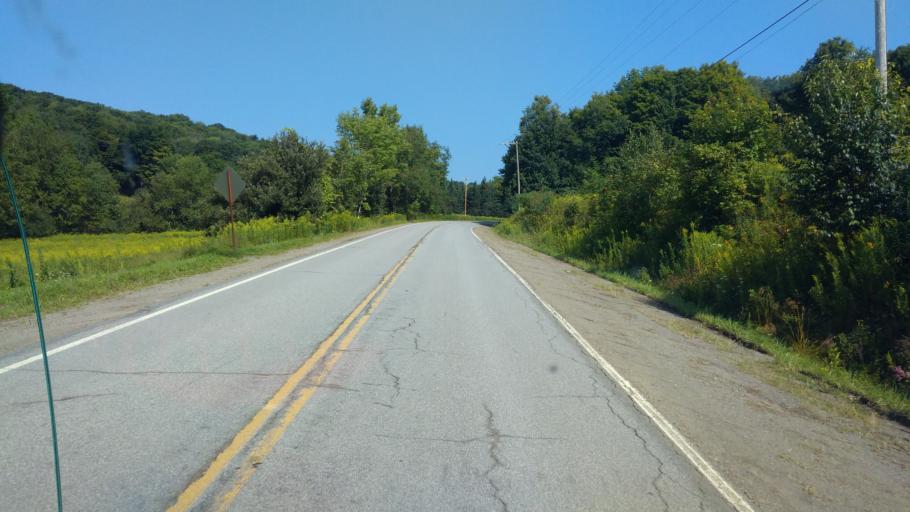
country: US
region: New York
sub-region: Allegany County
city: Bolivar
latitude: 42.1068
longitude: -78.1761
